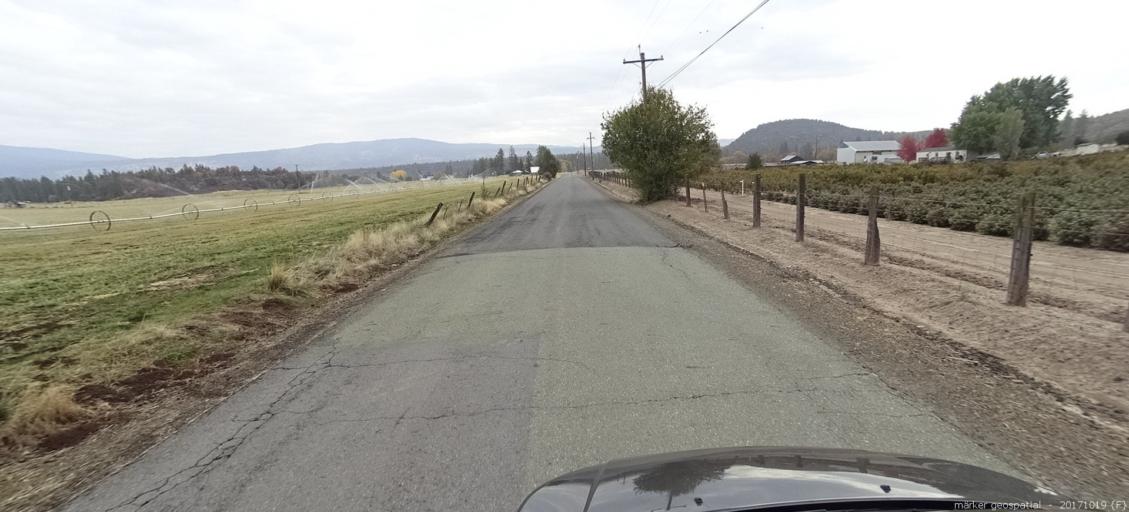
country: US
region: California
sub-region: Shasta County
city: Burney
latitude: 41.0659
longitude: -121.3433
